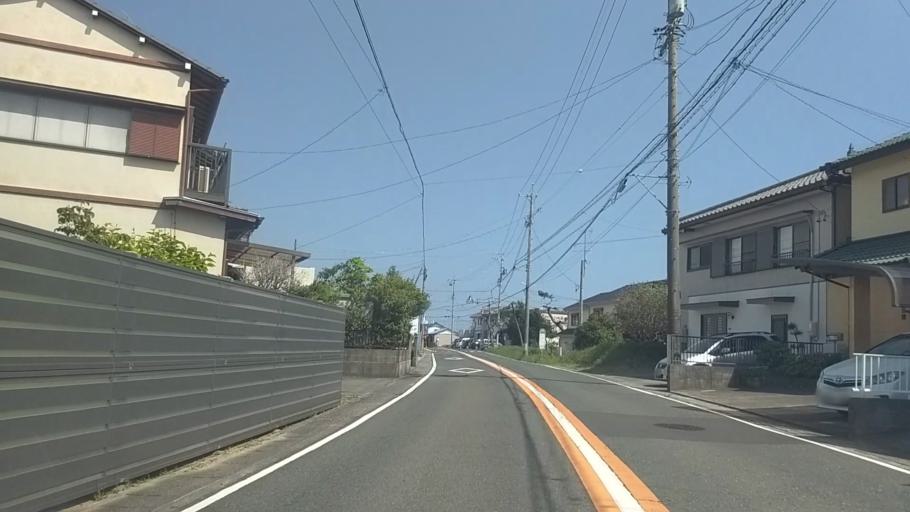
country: JP
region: Shizuoka
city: Hamamatsu
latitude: 34.6847
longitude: 137.6730
